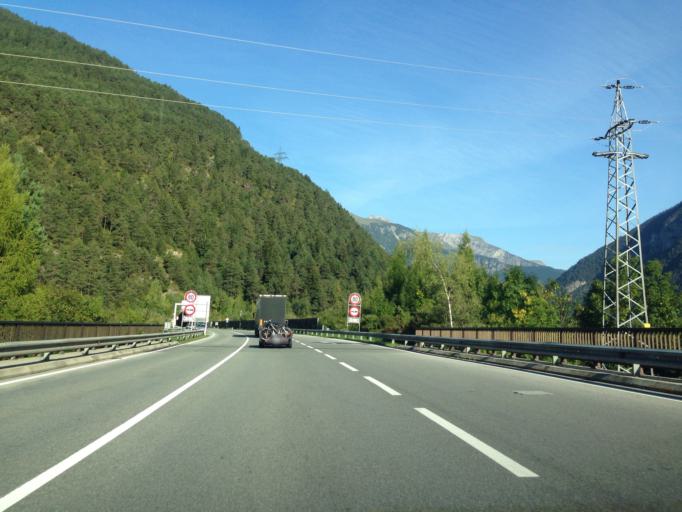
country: AT
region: Tyrol
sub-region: Politischer Bezirk Imst
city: Nassereith
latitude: 47.3051
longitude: 10.8412
